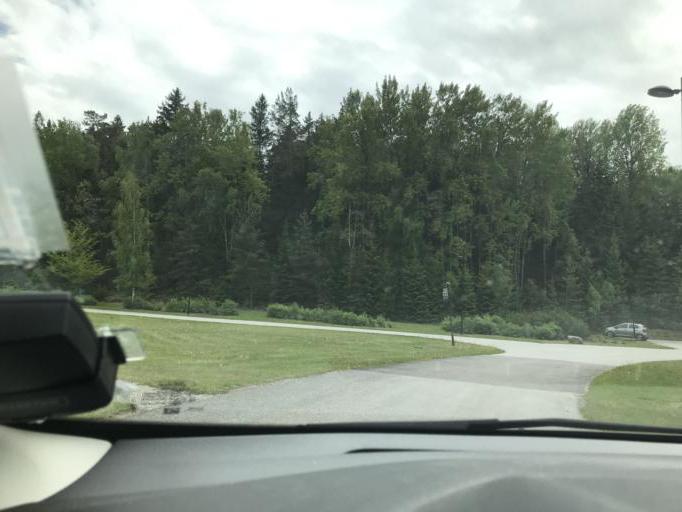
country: SE
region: Stockholm
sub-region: Botkyrka Kommun
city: Alby
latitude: 59.2187
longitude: 17.8502
